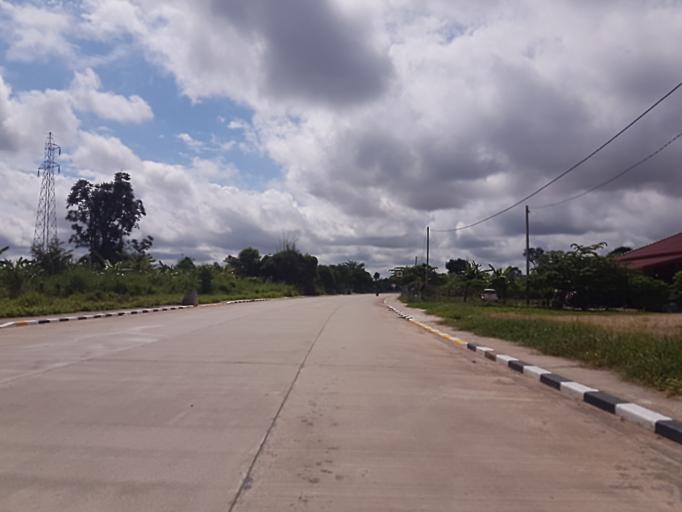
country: TH
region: Nong Khai
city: Nong Khai
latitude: 17.9066
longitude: 102.7047
